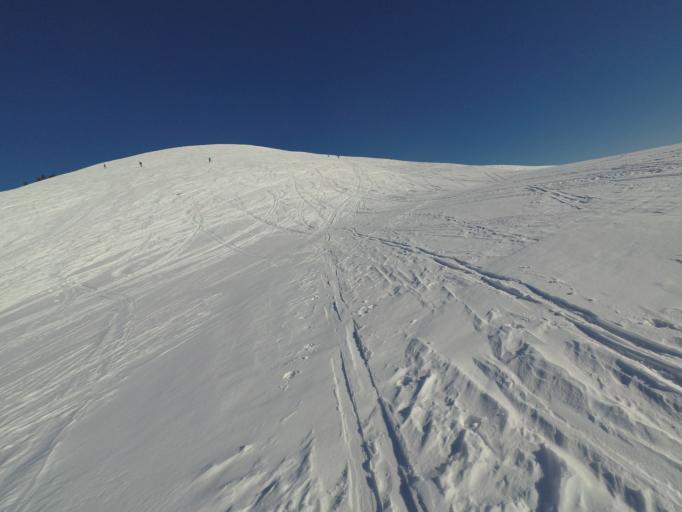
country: AT
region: Salzburg
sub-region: Politischer Bezirk Salzburg-Umgebung
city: Hintersee
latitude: 47.6384
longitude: 13.2695
